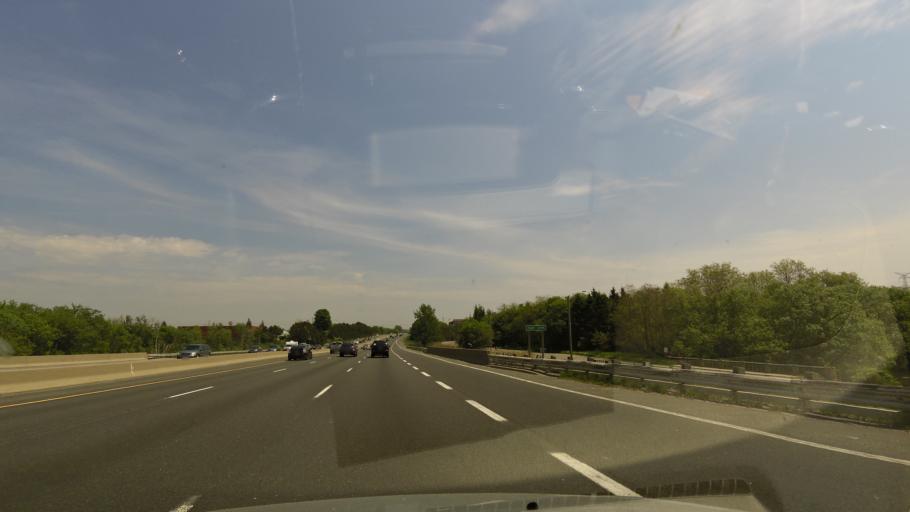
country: CA
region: Ontario
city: Oshawa
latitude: 43.8988
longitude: -78.6743
